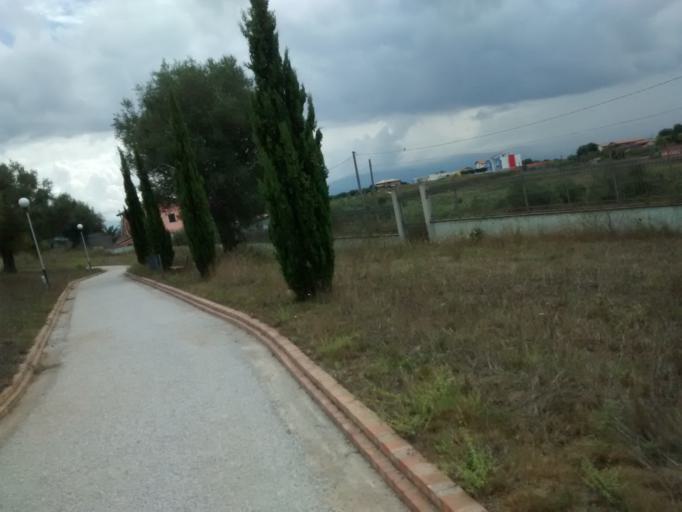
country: IT
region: Calabria
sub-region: Provincia di Vibo-Valentia
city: Vibo Valentia
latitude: 38.6628
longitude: 16.0783
